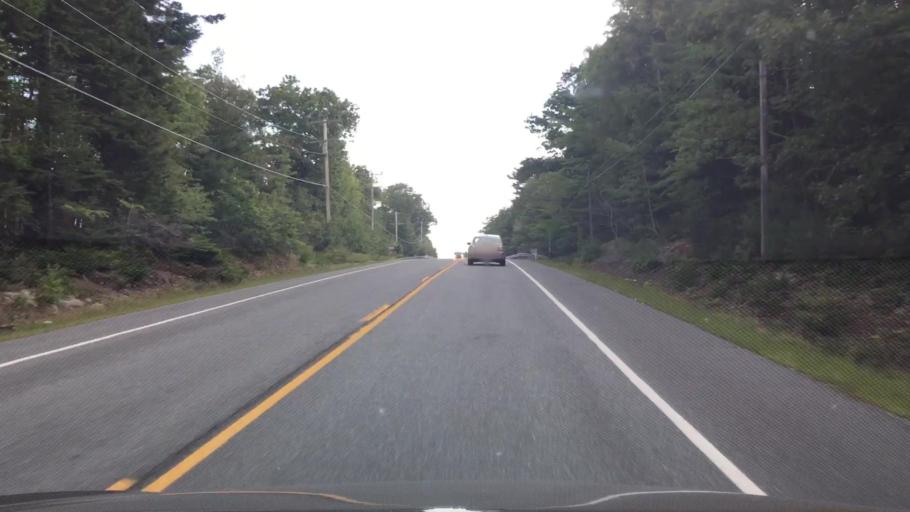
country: US
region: Maine
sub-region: Hancock County
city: Surry
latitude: 44.4521
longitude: -68.5556
